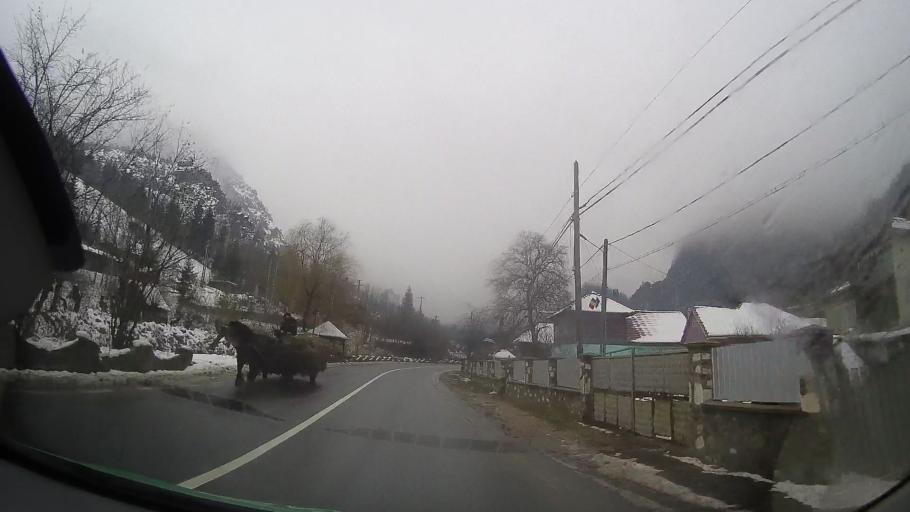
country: RO
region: Neamt
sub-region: Comuna Bicaz Chei
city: Bicaz Chei
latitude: 46.8244
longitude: 25.8593
